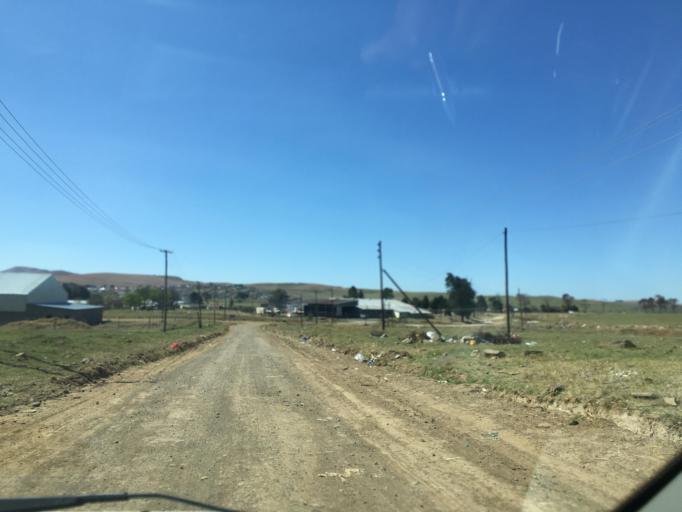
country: ZA
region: Eastern Cape
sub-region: Chris Hani District Municipality
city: Elliot
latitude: -31.3393
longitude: 27.8406
